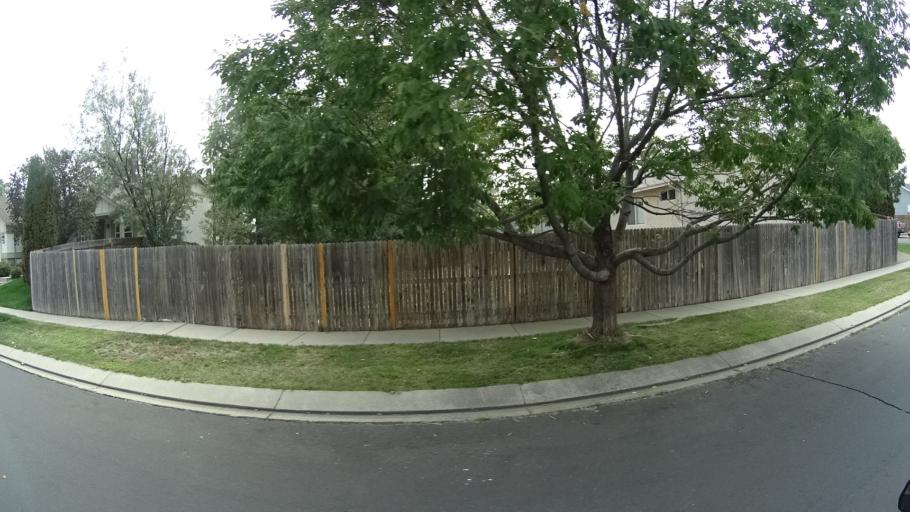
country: US
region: Colorado
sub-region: El Paso County
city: Cimarron Hills
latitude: 38.8232
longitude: -104.7372
